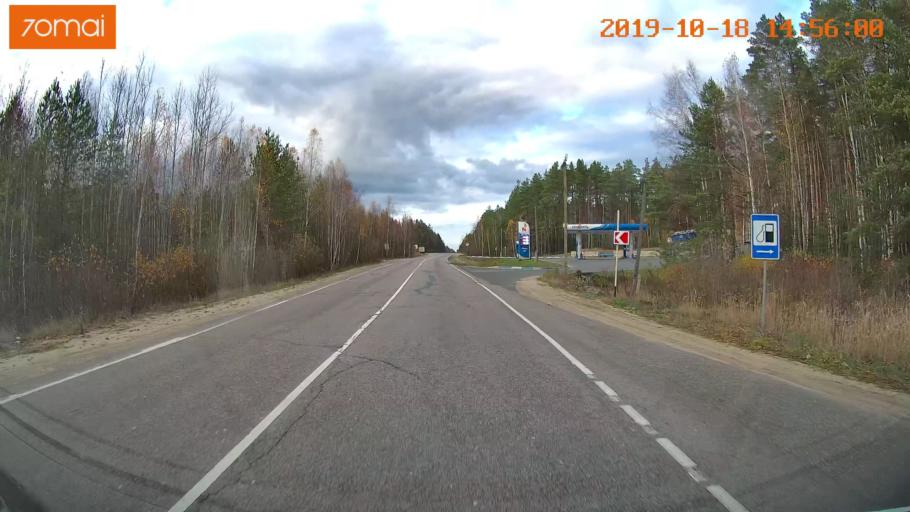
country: RU
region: Vladimir
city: Kurlovo
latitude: 55.4593
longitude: 40.5895
